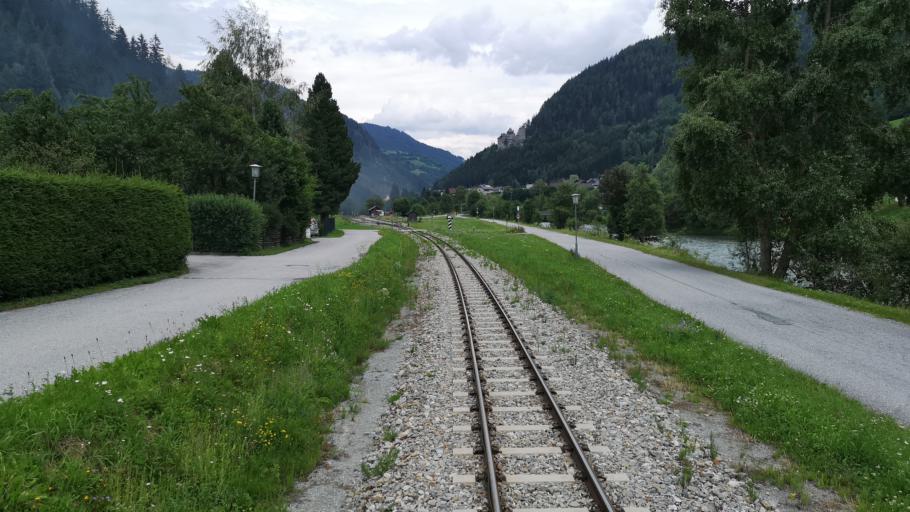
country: AT
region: Salzburg
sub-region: Politischer Bezirk Tamsweg
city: Ramingstein
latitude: 47.0749
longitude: 13.8265
